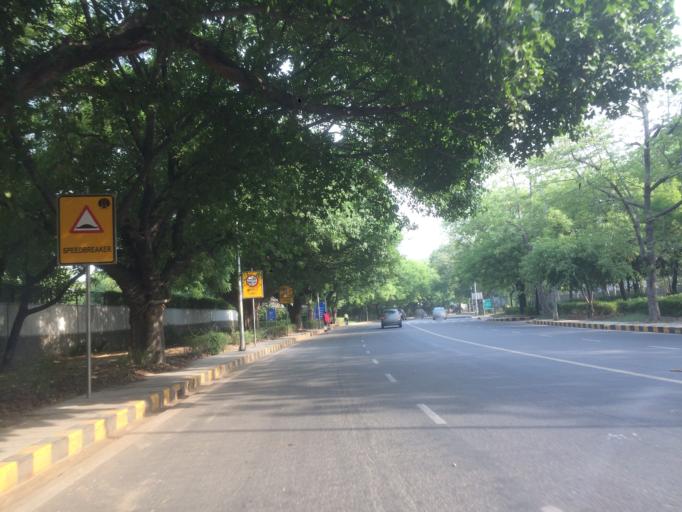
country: IN
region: NCT
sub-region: New Delhi
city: New Delhi
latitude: 28.5866
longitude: 77.1831
